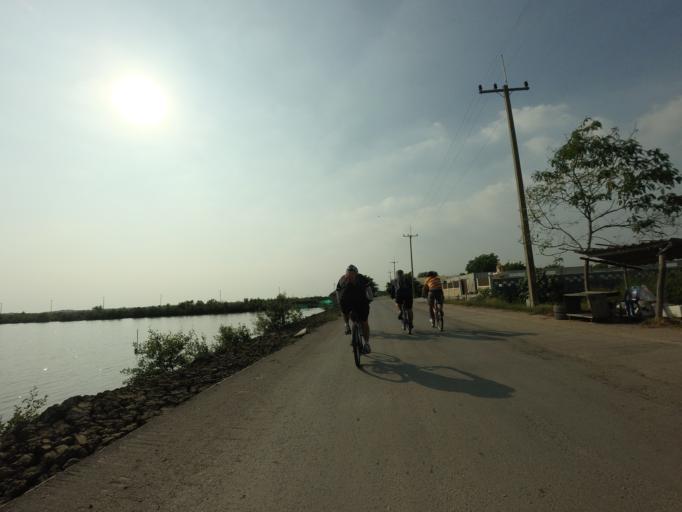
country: TH
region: Samut Sakhon
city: Samut Sakhon
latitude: 13.4981
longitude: 100.3463
